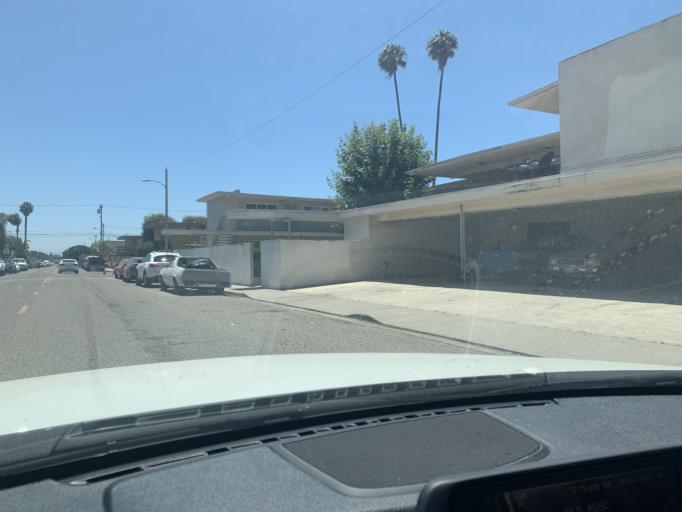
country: US
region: California
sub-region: Ventura County
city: Oxnard
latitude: 34.2132
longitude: -119.1922
